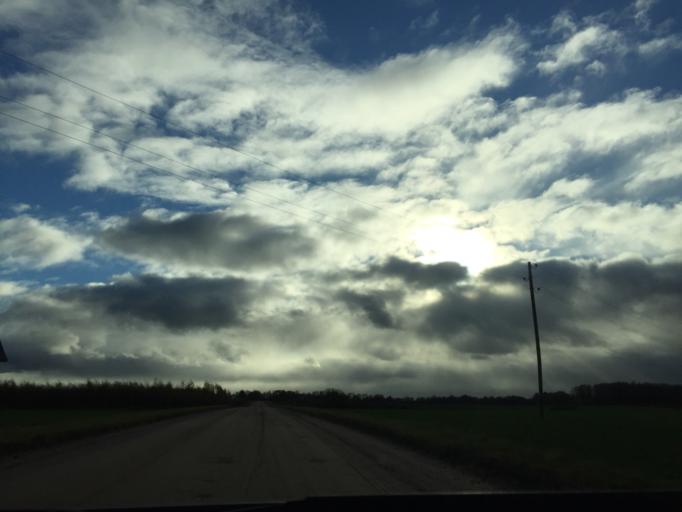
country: LV
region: Tukuma Rajons
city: Tukums
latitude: 56.9327
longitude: 22.9534
